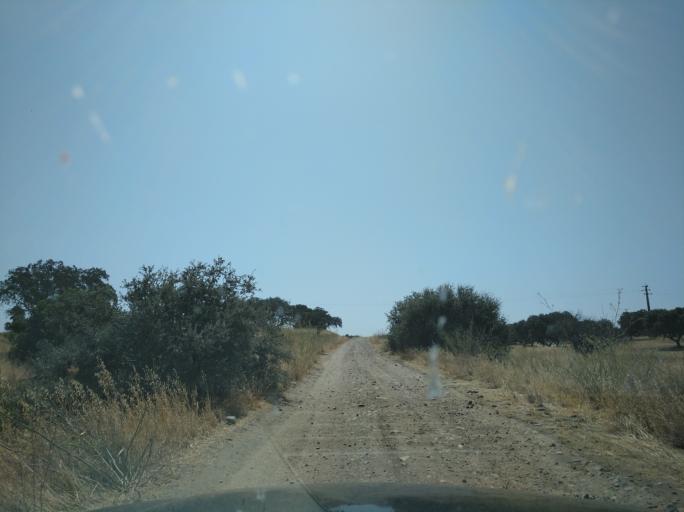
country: PT
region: Portalegre
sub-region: Campo Maior
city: Campo Maior
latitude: 39.0306
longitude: -6.9797
